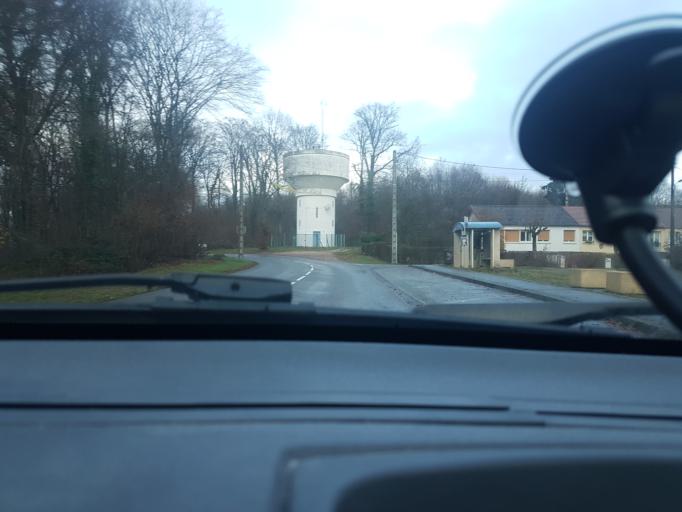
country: FR
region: Franche-Comte
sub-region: Territoire de Belfort
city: Bavilliers
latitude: 47.6082
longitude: 6.8417
